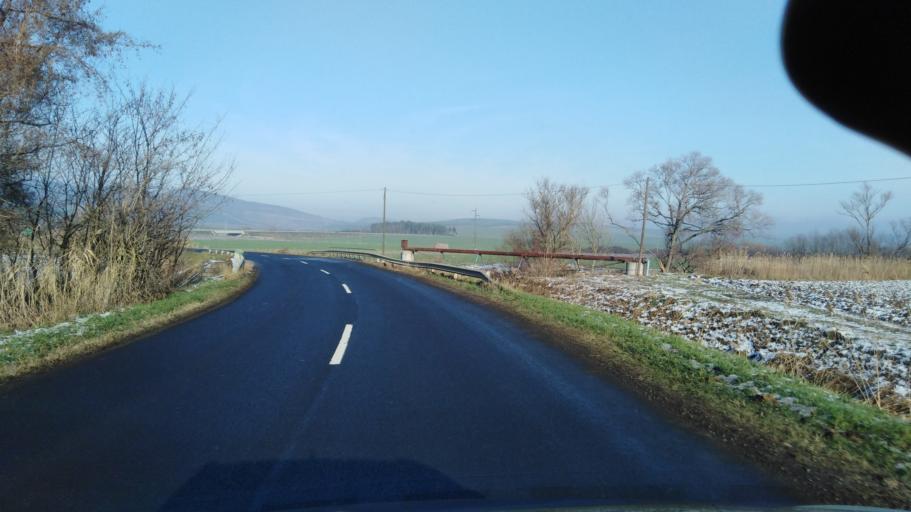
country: HU
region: Nograd
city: Paszto
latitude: 47.9398
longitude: 19.7065
